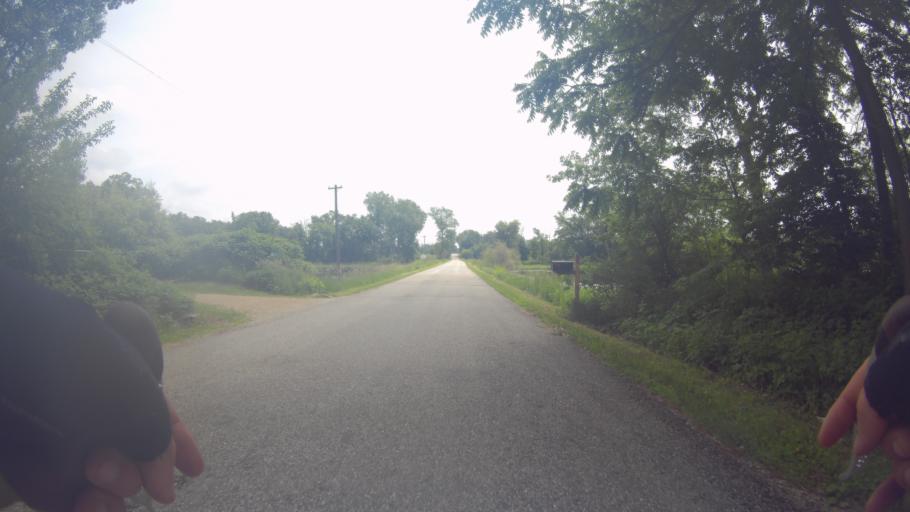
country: US
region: Wisconsin
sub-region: Jefferson County
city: Cambridge
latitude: 42.9682
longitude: -89.0052
